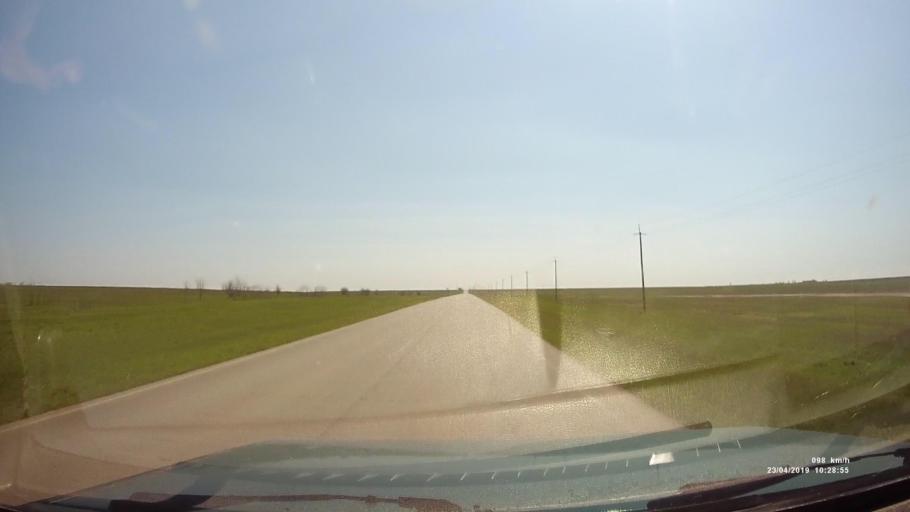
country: RU
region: Kalmykiya
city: Yashalta
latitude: 46.6020
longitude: 42.5167
